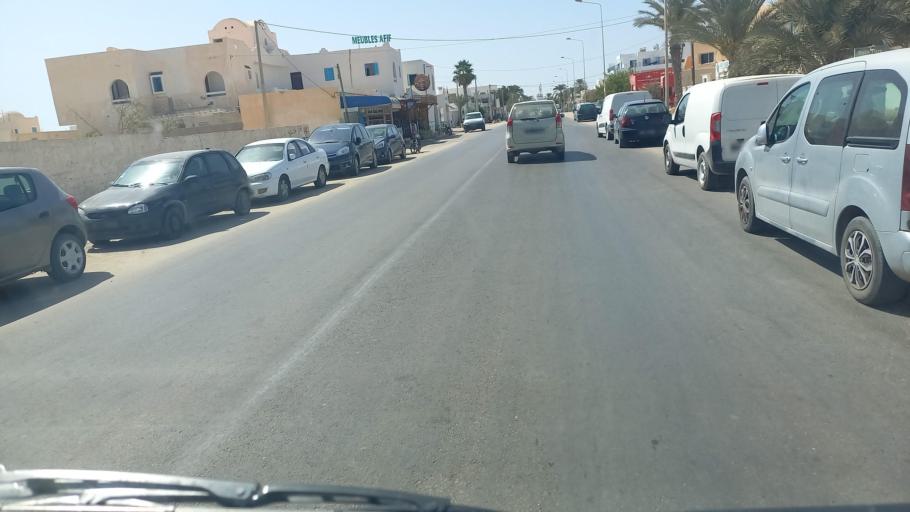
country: TN
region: Madanin
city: Houmt Souk
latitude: 33.8765
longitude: 10.8745
